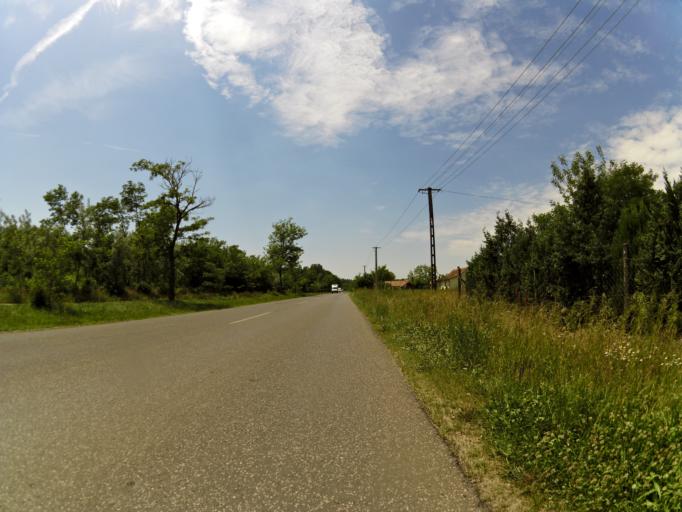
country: HU
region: Csongrad
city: Kistelek
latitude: 46.4866
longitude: 20.0215
